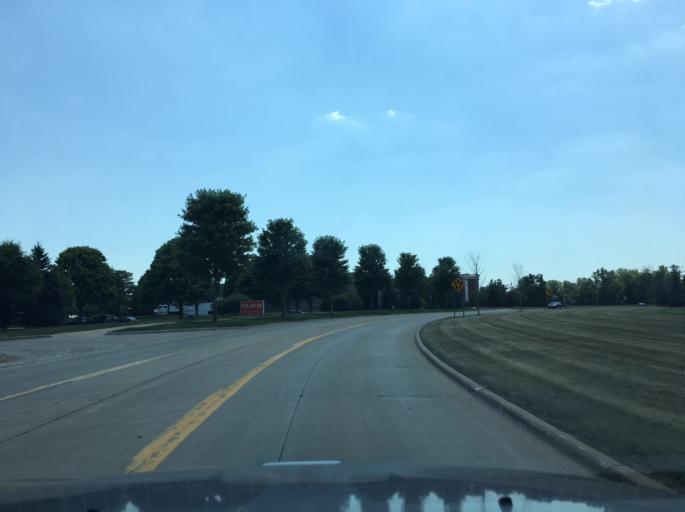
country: US
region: Michigan
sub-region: Macomb County
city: Shelby
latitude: 42.6767
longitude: -83.0124
